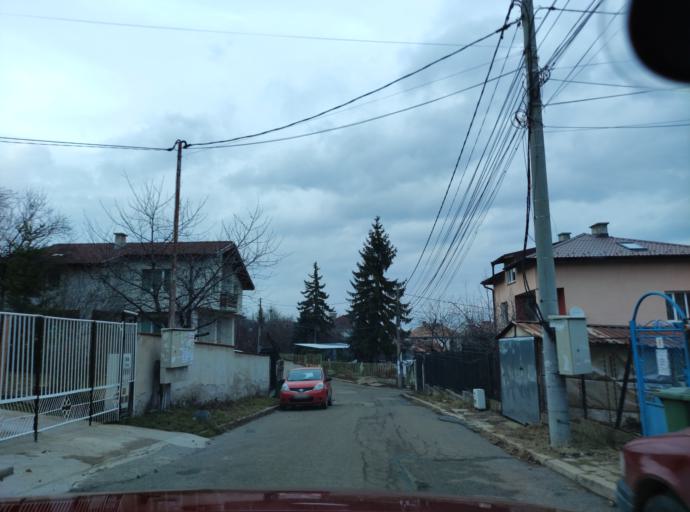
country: BG
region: Sofia-Capital
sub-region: Stolichna Obshtina
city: Sofia
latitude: 42.6140
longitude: 23.3371
